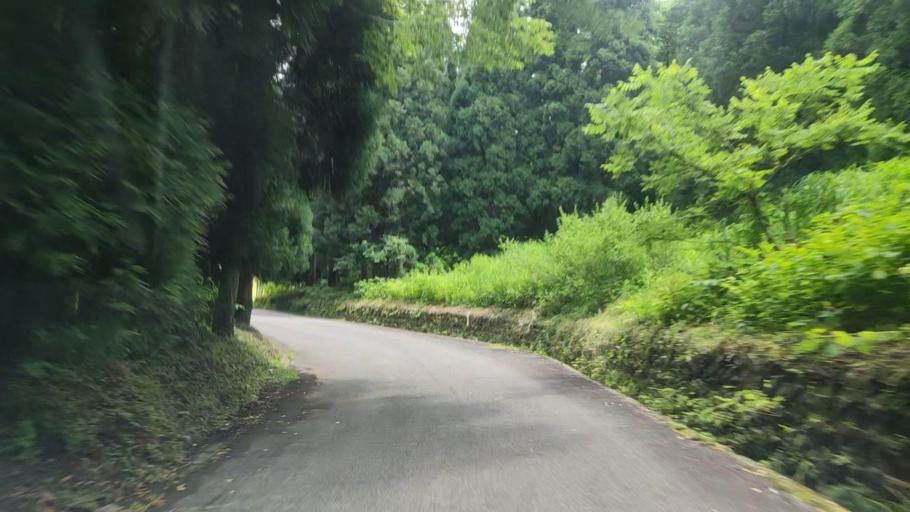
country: JP
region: Fukui
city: Ono
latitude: 35.8091
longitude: 136.4651
